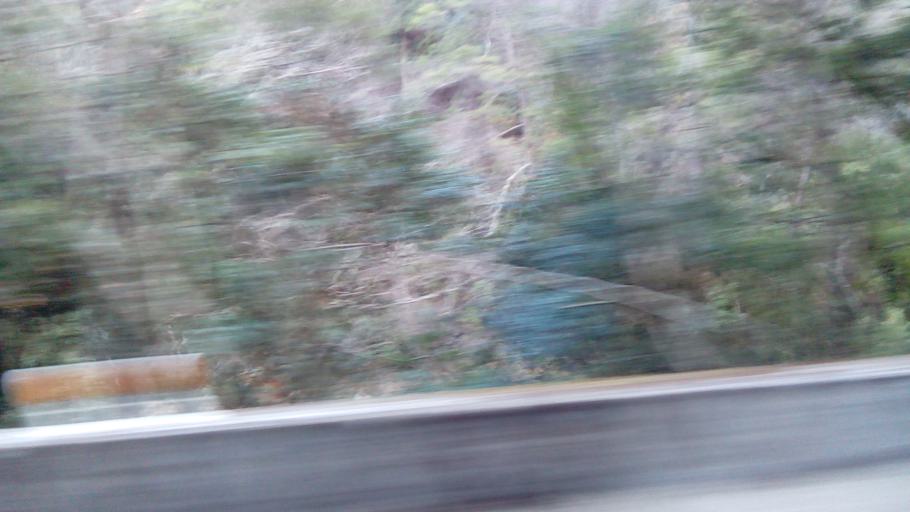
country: TW
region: Taiwan
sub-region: Hualien
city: Hualian
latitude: 24.3445
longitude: 121.3103
